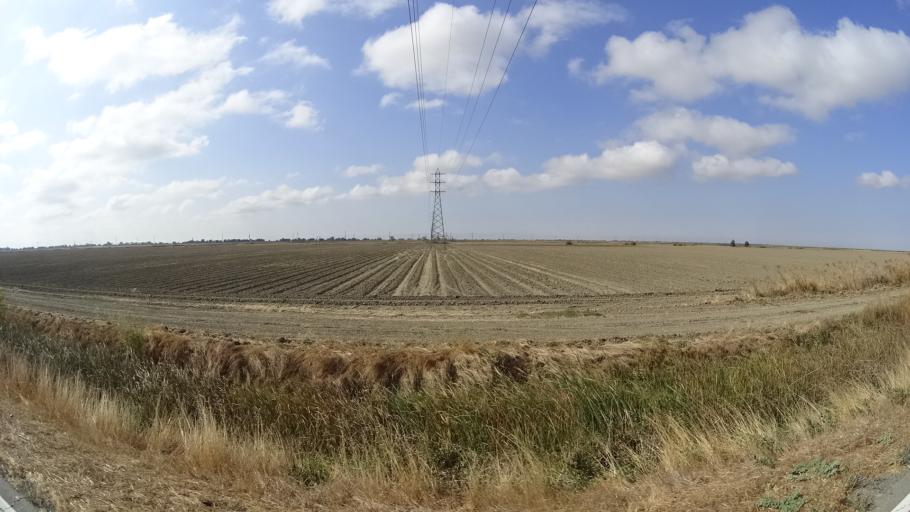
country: US
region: California
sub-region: Yolo County
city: Woodland
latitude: 38.8131
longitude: -121.7374
